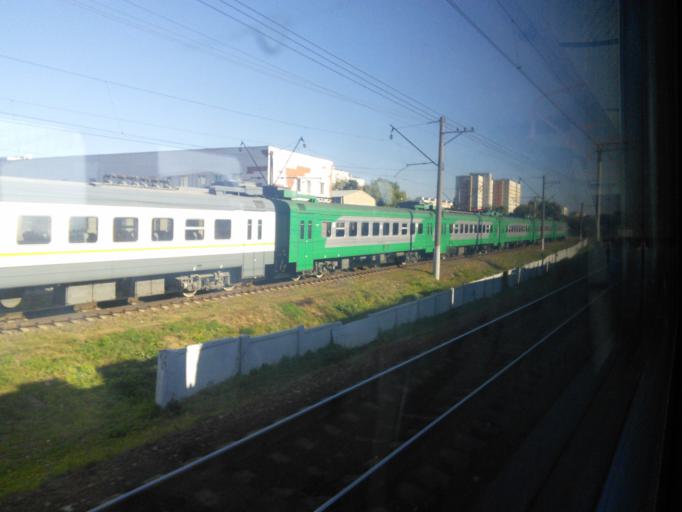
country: RU
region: Moscow
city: Mar'ino
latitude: 55.6678
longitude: 37.7243
